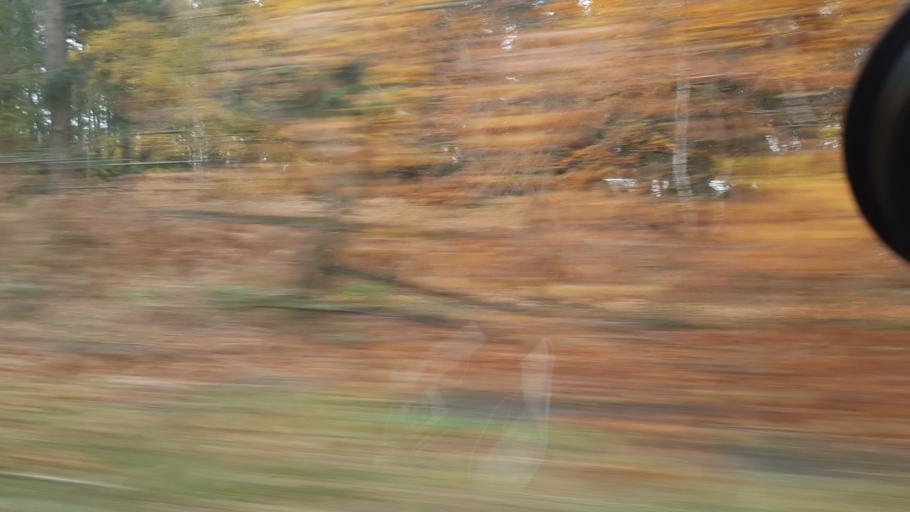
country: GB
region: England
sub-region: Hampshire
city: Yateley
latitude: 51.3138
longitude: -0.8152
